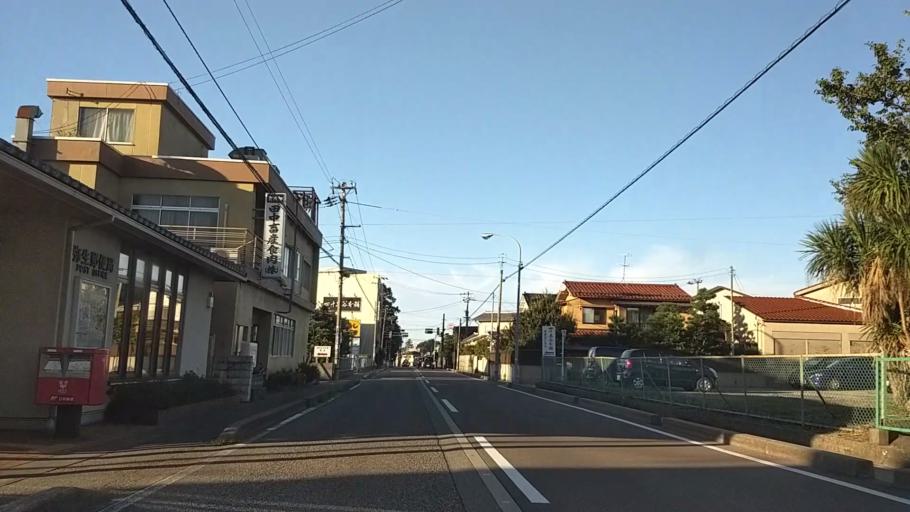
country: JP
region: Ishikawa
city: Nonoichi
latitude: 36.5485
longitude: 136.6493
